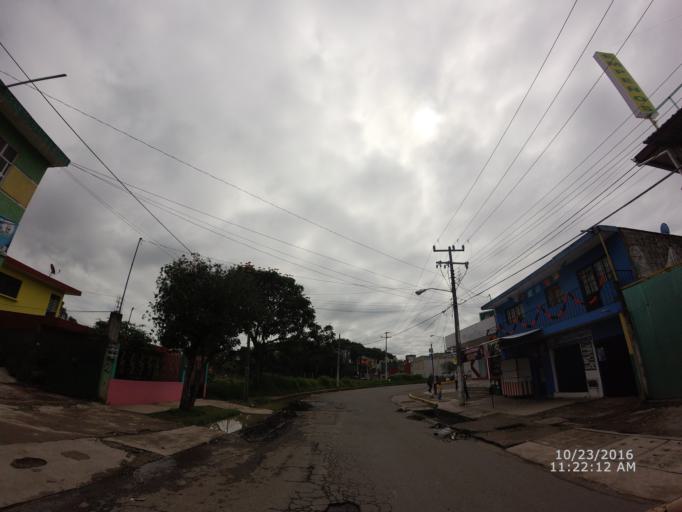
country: MX
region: Veracruz
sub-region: Tlalnelhuayocan
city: Guadalupe Victoria
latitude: 19.5504
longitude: -96.9480
